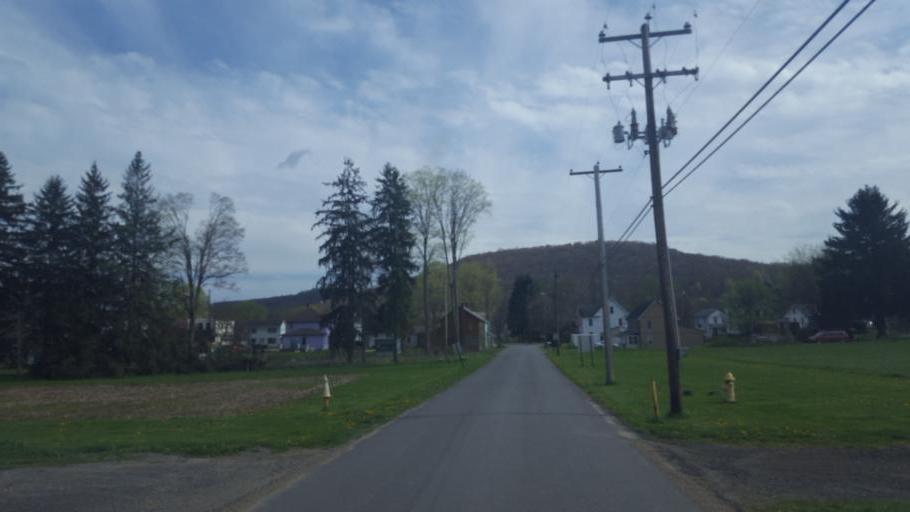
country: US
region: Pennsylvania
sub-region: Venango County
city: Sugarcreek
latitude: 41.3681
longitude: -79.9308
